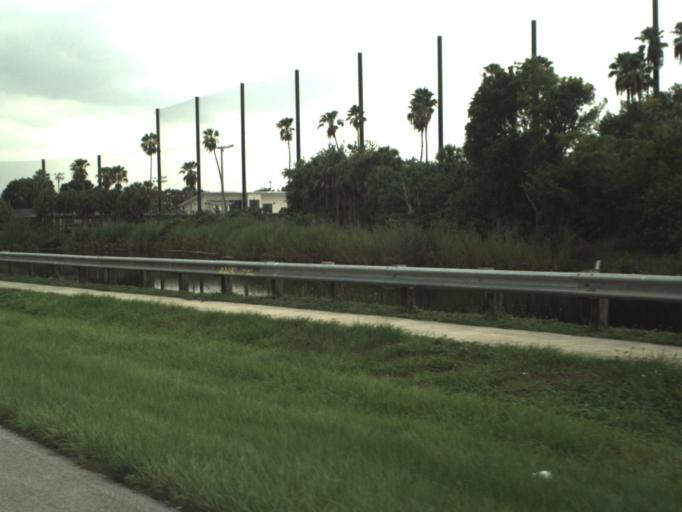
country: US
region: Florida
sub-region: Broward County
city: Sunshine Ranches
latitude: 26.0189
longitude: -80.3124
